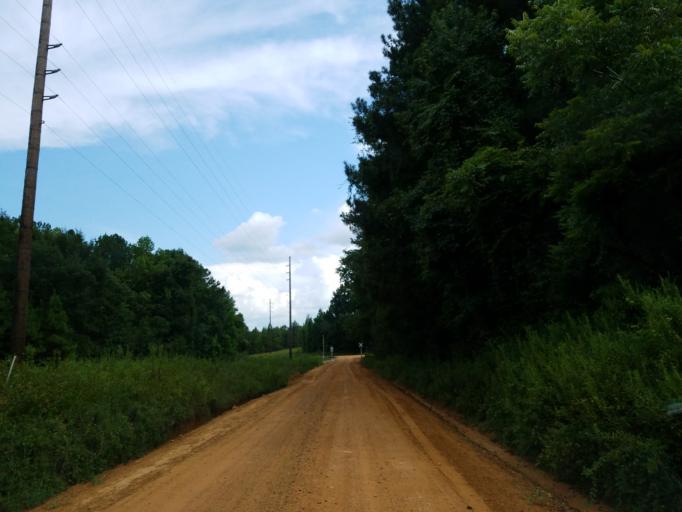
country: US
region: Georgia
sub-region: Dooly County
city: Unadilla
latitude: 32.2891
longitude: -83.7184
